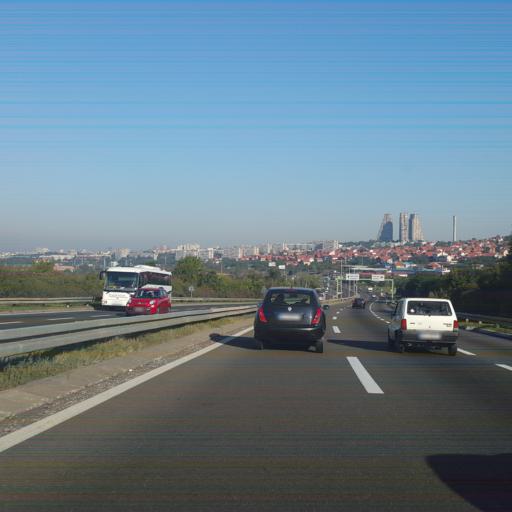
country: RS
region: Central Serbia
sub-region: Belgrade
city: Zvezdara
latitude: 44.7676
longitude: 20.5236
